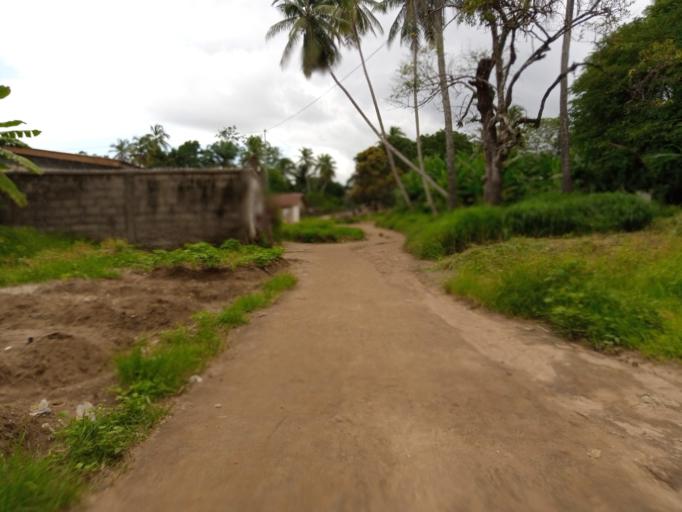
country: SL
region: Northern Province
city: Masoyila
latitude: 8.5739
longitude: -13.1617
